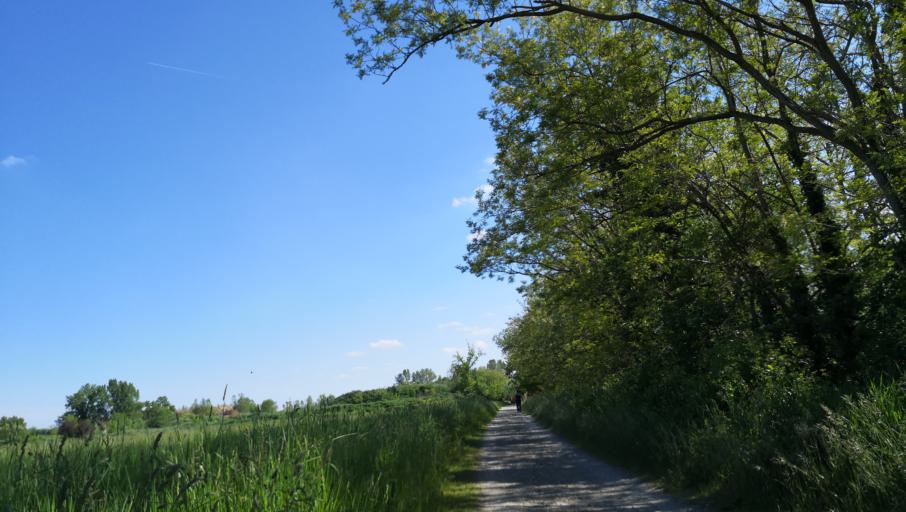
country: FR
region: Midi-Pyrenees
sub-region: Departement de la Haute-Garonne
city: Aucamville
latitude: 43.6596
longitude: 1.4073
